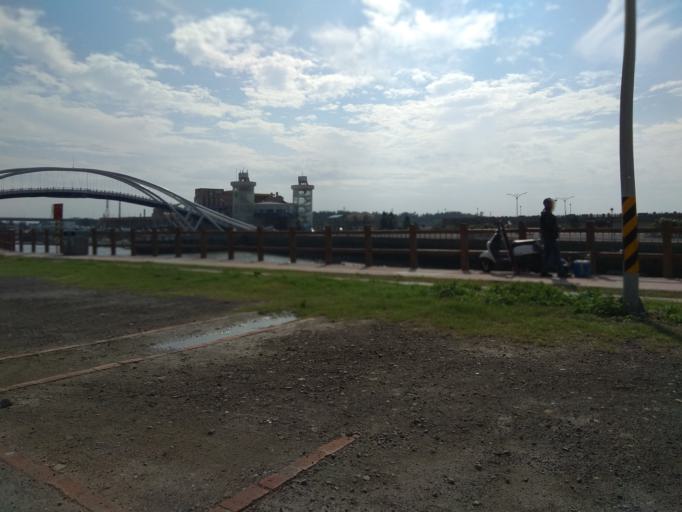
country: TW
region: Taiwan
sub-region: Hsinchu
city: Zhubei
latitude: 24.9894
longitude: 121.0133
